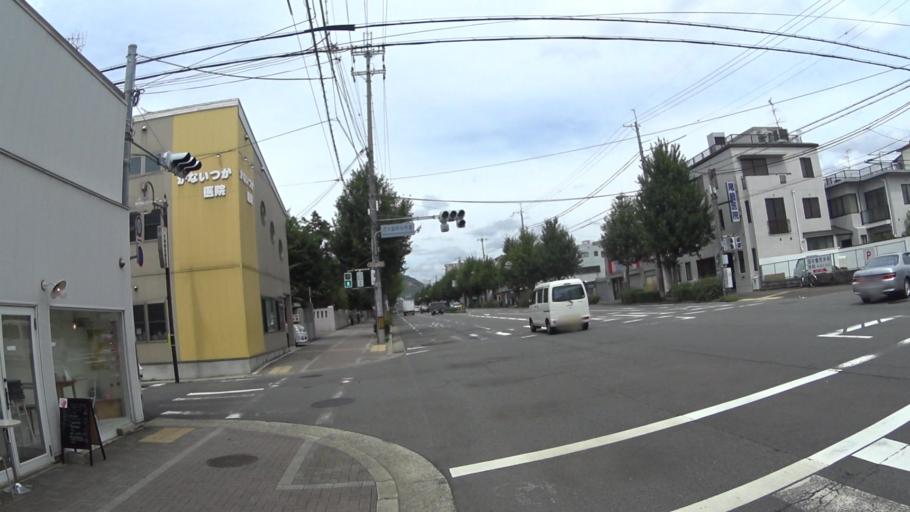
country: JP
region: Kyoto
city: Kyoto
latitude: 35.0210
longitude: 135.7317
